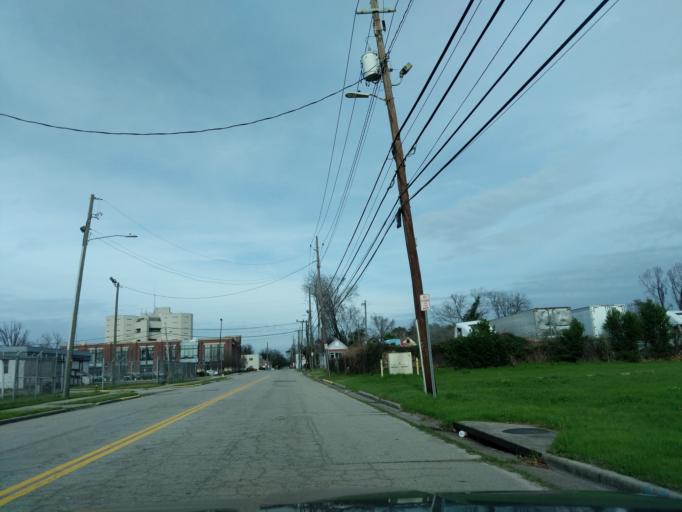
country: US
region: Georgia
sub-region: Richmond County
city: Augusta
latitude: 33.4631
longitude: -81.9607
